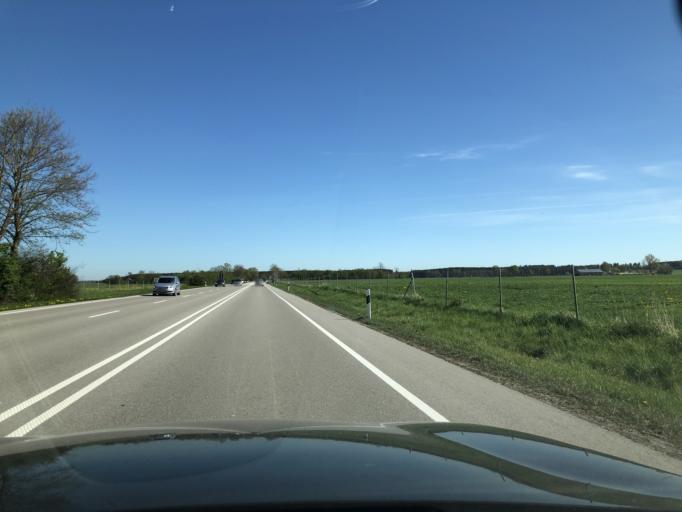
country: DE
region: Bavaria
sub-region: Swabia
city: Rieden
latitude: 47.9654
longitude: 10.6851
